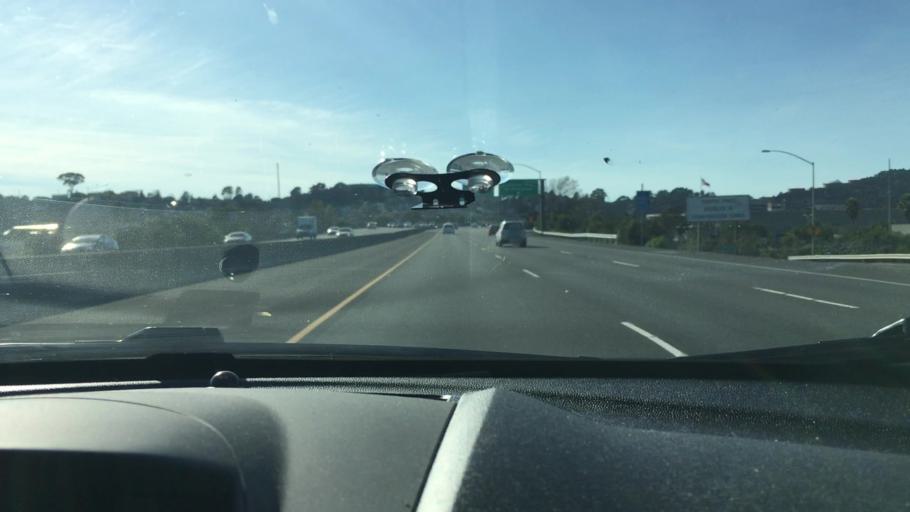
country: US
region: California
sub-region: Contra Costa County
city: Richmond
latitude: 37.9272
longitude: -122.3755
